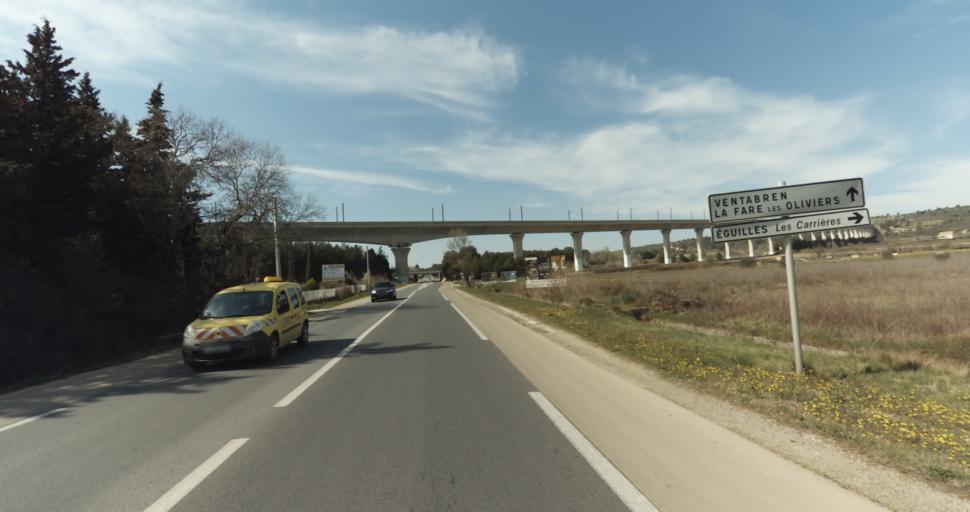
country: FR
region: Provence-Alpes-Cote d'Azur
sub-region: Departement des Bouches-du-Rhone
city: Eguilles
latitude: 43.5460
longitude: 5.3336
